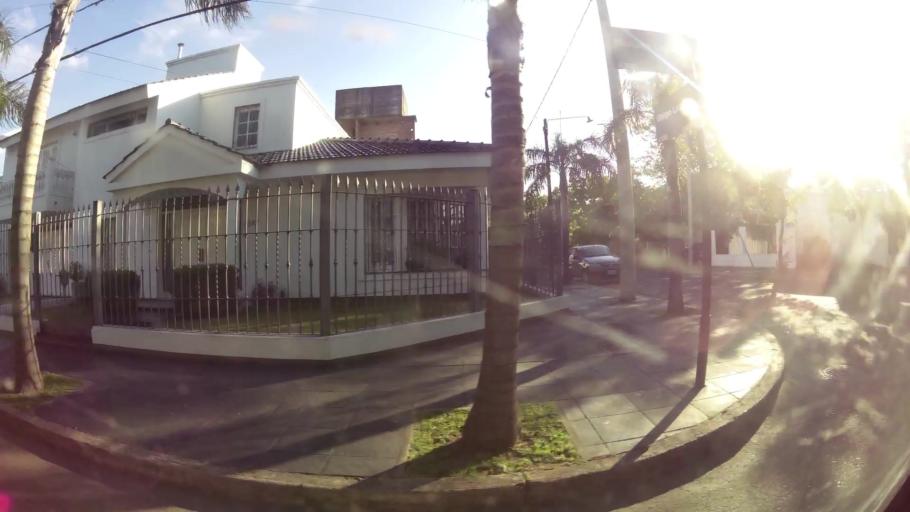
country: AR
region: Cordoba
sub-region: Departamento de Capital
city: Cordoba
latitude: -31.3771
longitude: -64.2414
